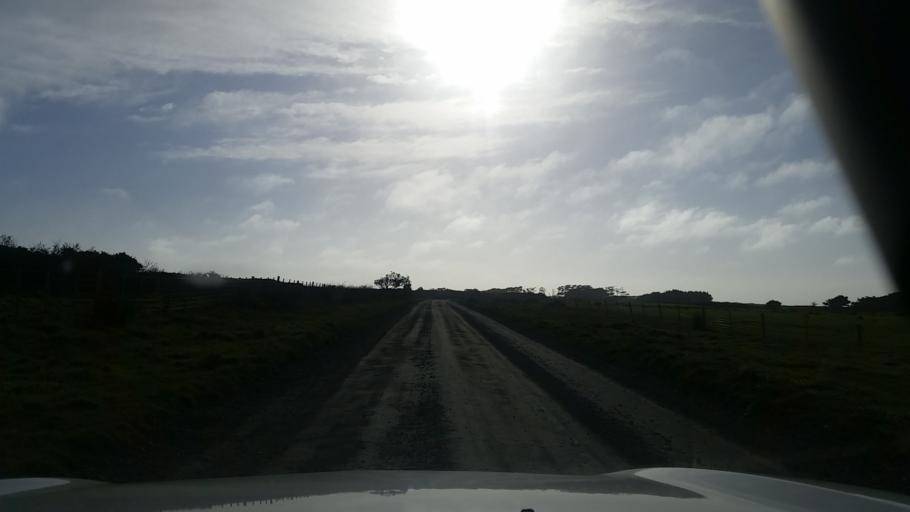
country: NZ
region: Chatham Islands
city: Waitangi
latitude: -43.8471
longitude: -176.5370
